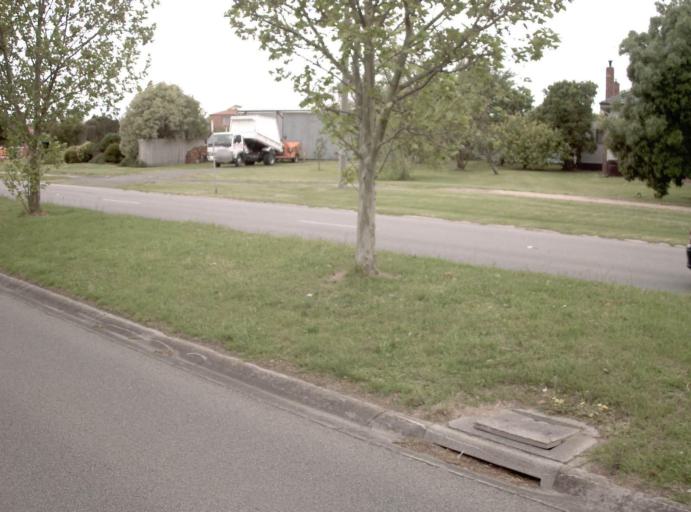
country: AU
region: Victoria
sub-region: Knox
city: Wantirna
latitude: -37.8509
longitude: 145.2239
